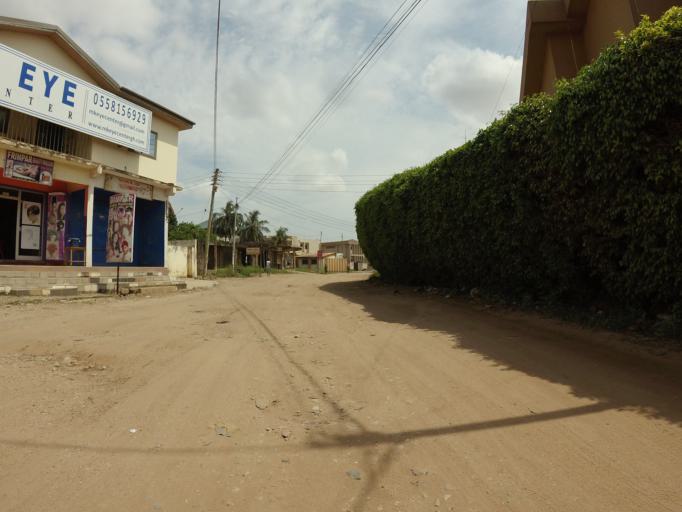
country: GH
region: Greater Accra
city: Dome
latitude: 5.6366
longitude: -0.2379
